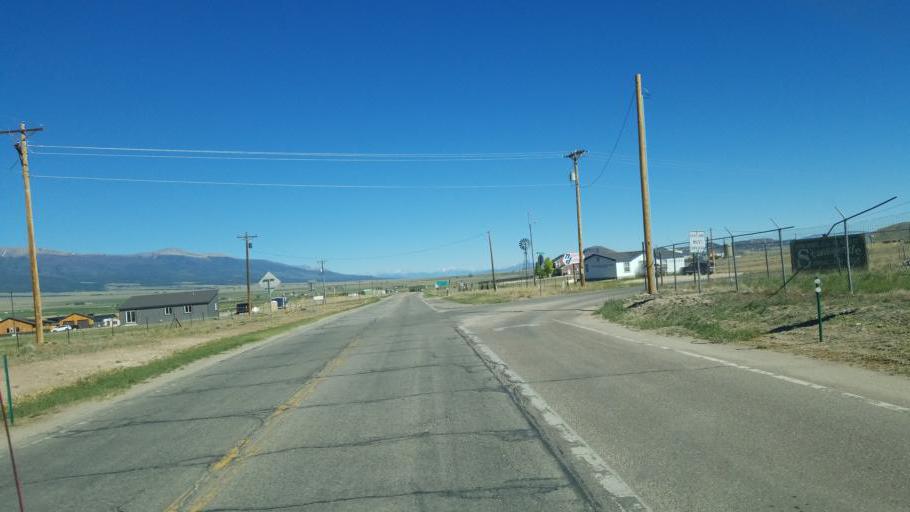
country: US
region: Colorado
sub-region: Custer County
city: Westcliffe
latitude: 38.1393
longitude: -105.4687
